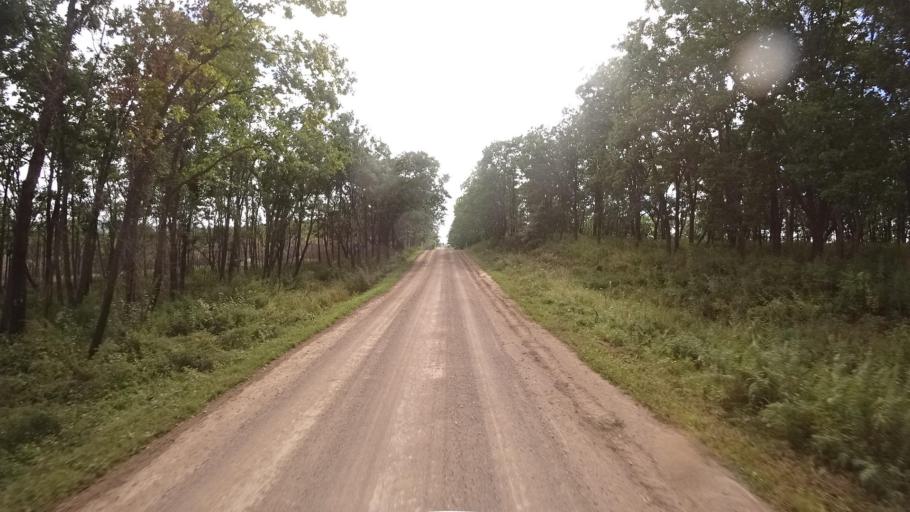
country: RU
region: Primorskiy
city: Dostoyevka
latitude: 44.3449
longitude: 133.5125
